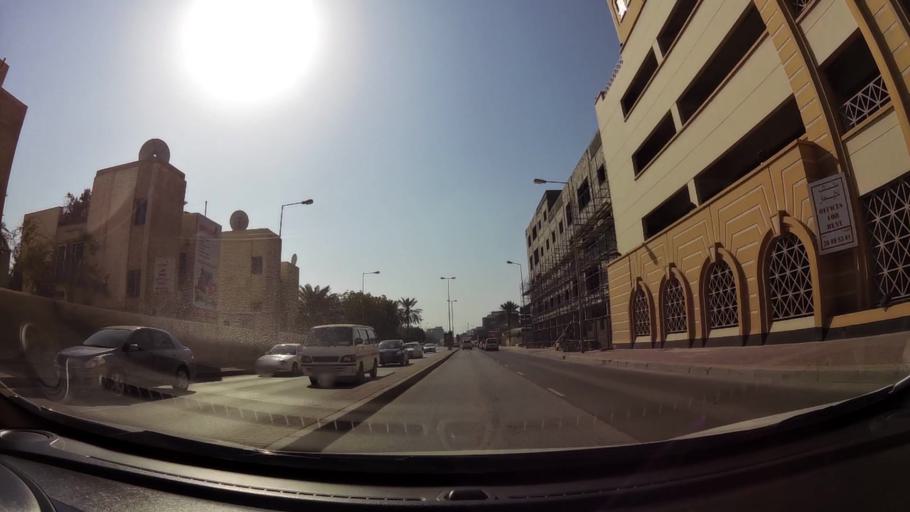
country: BH
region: Manama
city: Manama
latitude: 26.2151
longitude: 50.5812
